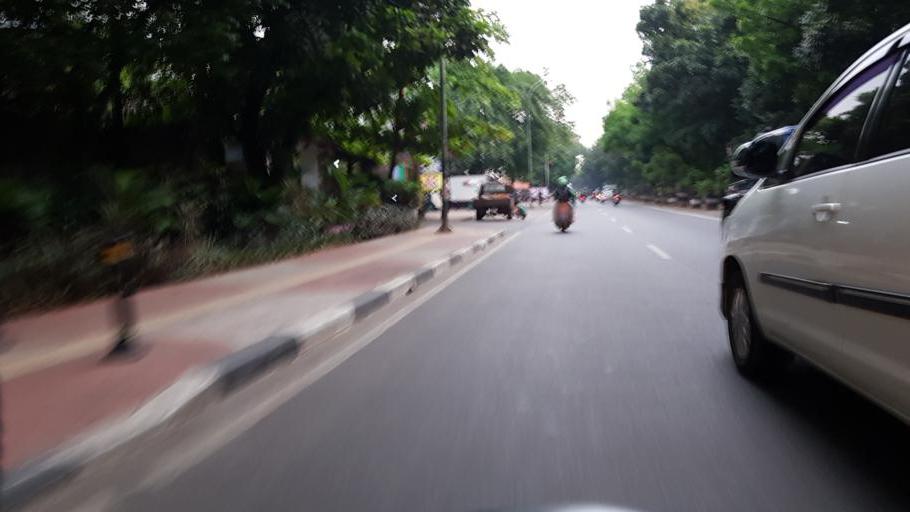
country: ID
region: Jakarta Raya
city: Jakarta
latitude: -6.3069
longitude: 106.8926
